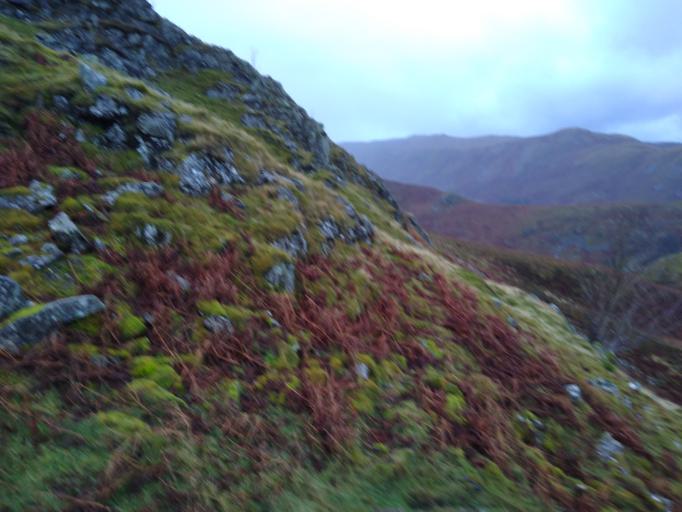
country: GB
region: England
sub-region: Cumbria
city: Penrith
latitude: 54.5623
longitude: -2.8712
